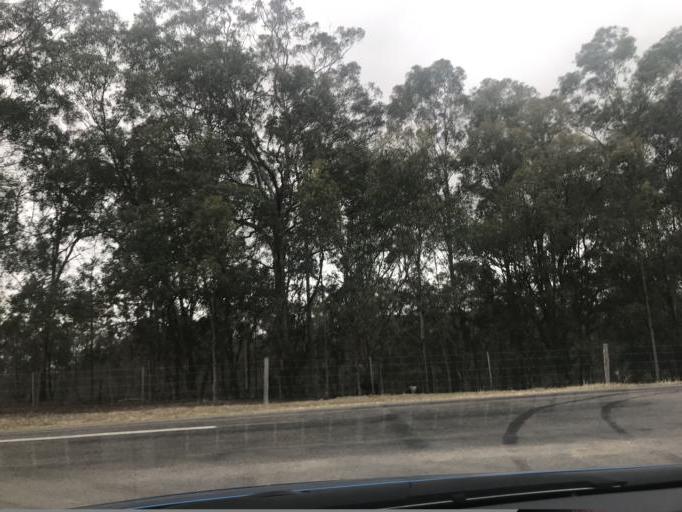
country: AU
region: New South Wales
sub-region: Cessnock
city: Cessnock
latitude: -32.9051
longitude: 151.2876
